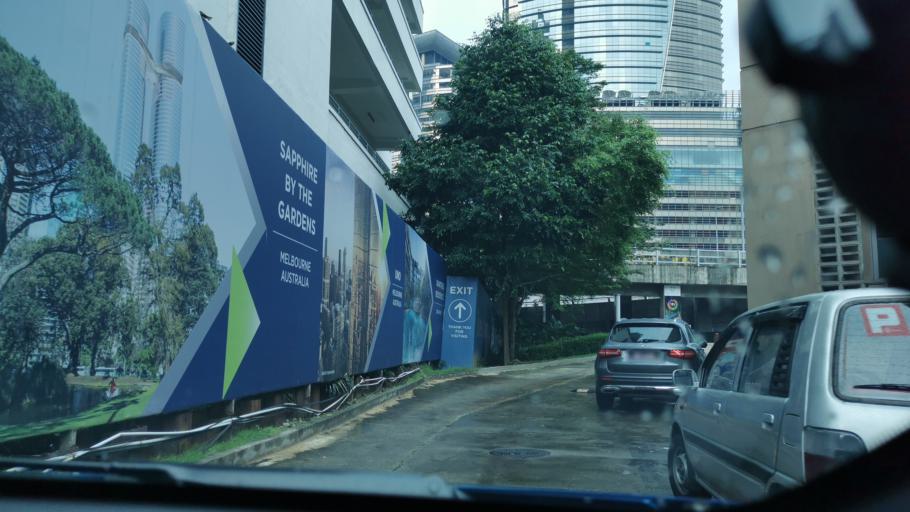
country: MY
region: Kuala Lumpur
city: Kuala Lumpur
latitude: 3.1163
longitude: 101.6739
